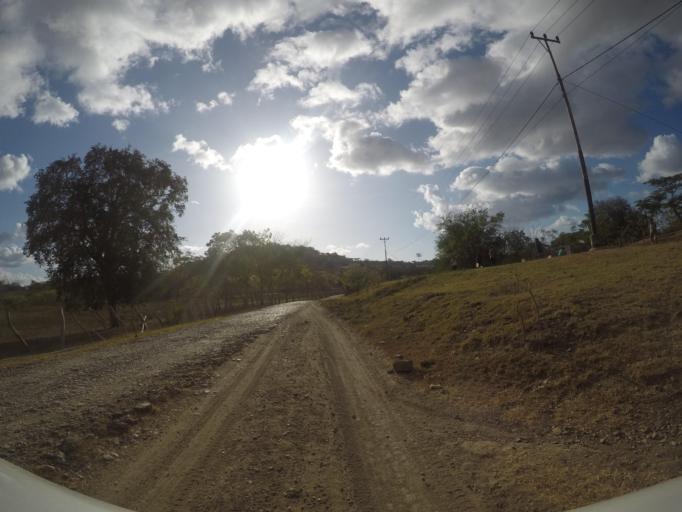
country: TL
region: Lautem
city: Lospalos
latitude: -8.4268
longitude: 126.8359
